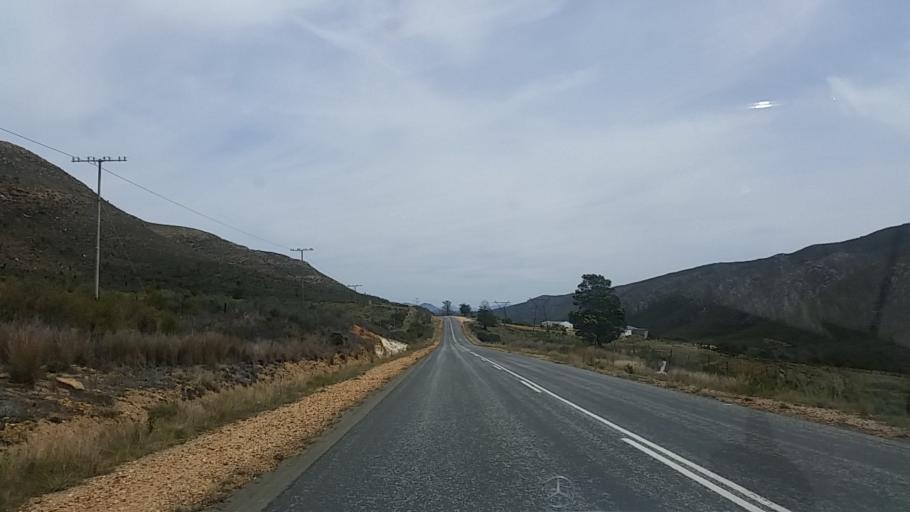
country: ZA
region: Western Cape
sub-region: Eden District Municipality
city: Knysna
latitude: -33.7436
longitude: 22.9965
